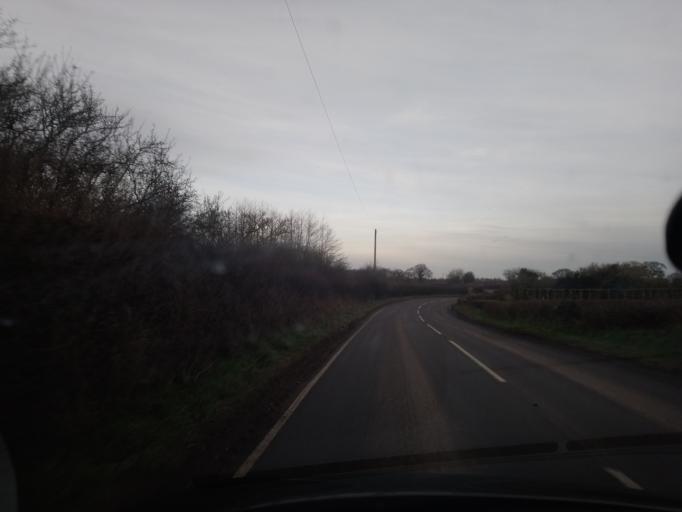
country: GB
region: England
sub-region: Shropshire
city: Whitchurch
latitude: 52.9397
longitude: -2.6824
